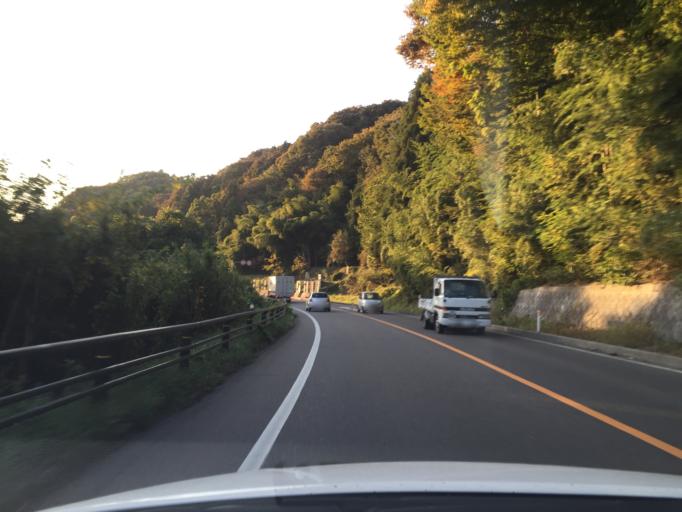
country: JP
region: Fukushima
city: Sukagawa
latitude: 37.3129
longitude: 140.4464
